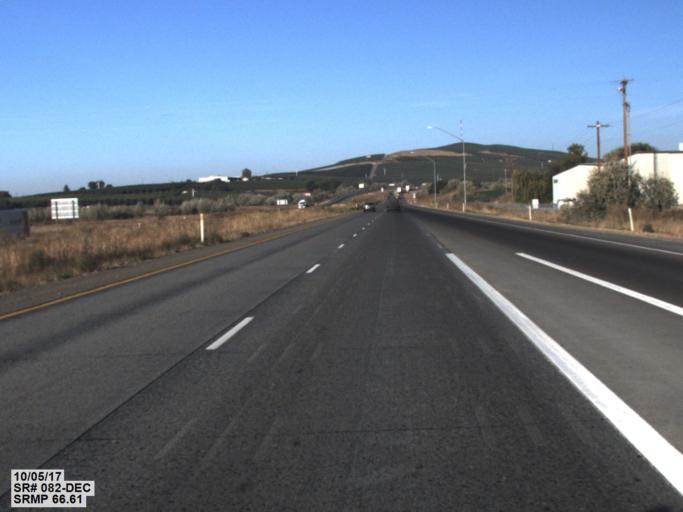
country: US
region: Washington
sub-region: Yakima County
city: Sunnyside
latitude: 46.3063
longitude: -120.0271
